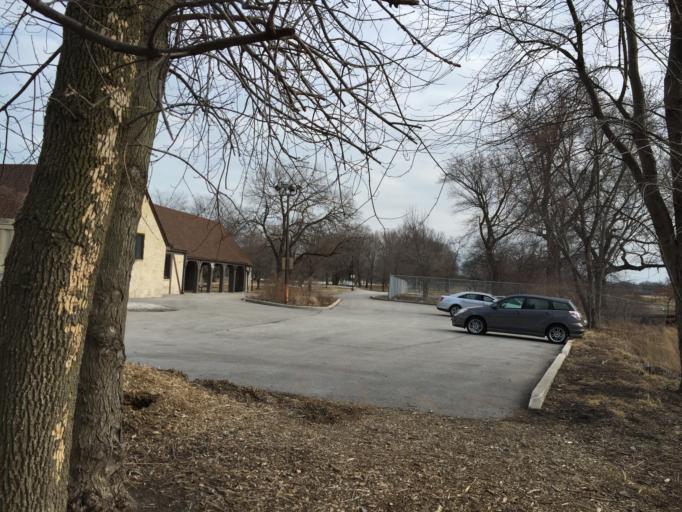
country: US
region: Illinois
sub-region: Cook County
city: Chicago
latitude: 41.7837
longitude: -87.5791
